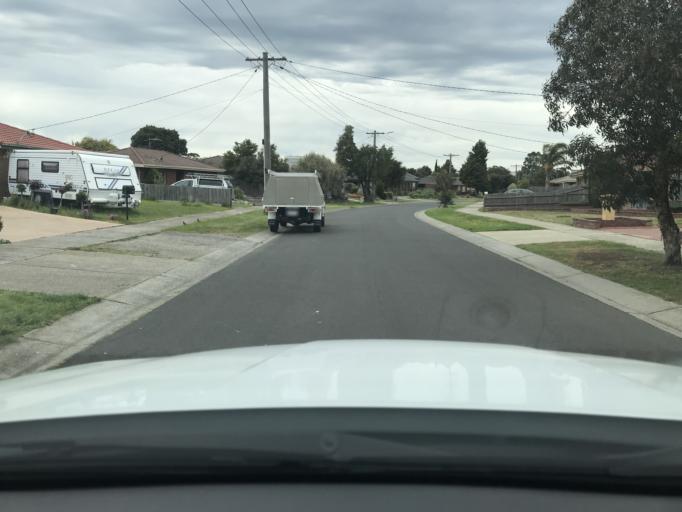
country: AU
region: Victoria
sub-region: Hume
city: Craigieburn
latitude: -37.6100
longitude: 144.9374
